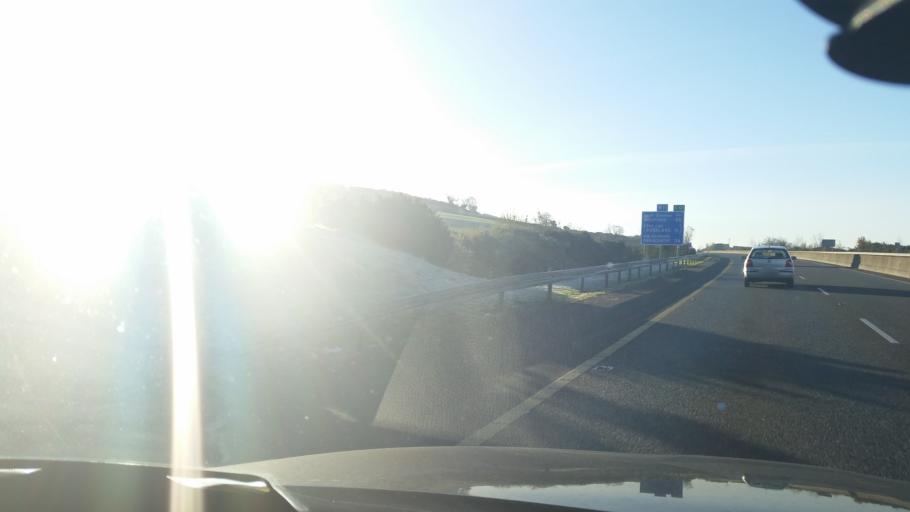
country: IE
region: Leinster
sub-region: Loch Garman
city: Gorey
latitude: 52.7039
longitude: -6.2618
